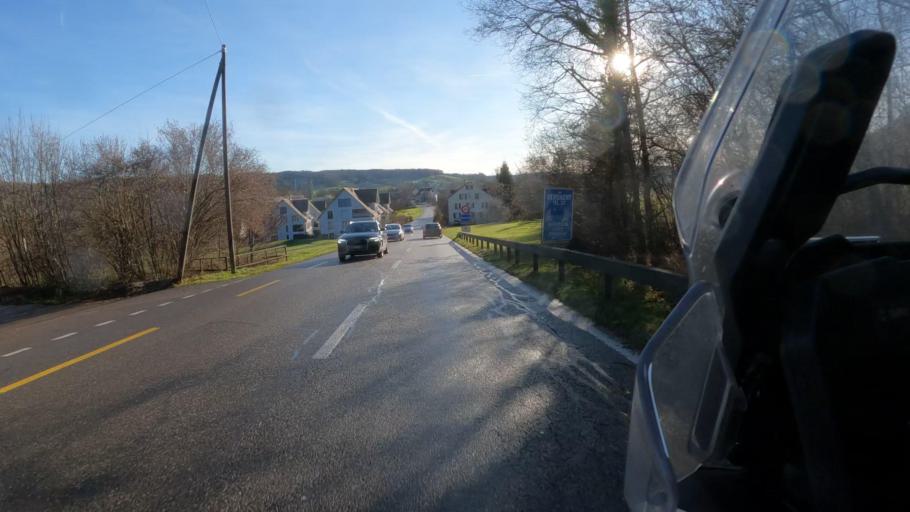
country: CH
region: Zurich
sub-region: Bezirk Buelach
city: Embrach / Kellersacker
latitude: 47.5132
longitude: 8.5856
